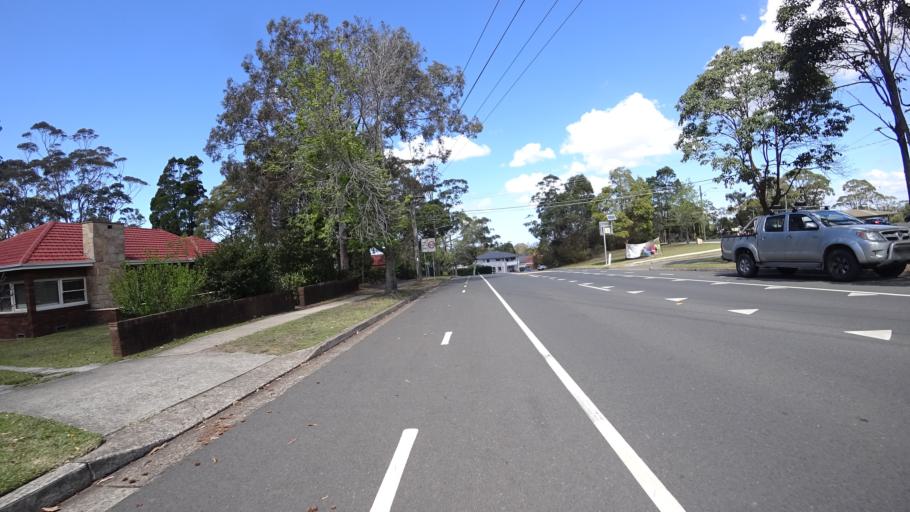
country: AU
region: New South Wales
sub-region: Warringah
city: Forestville
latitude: -33.7631
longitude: 151.2112
